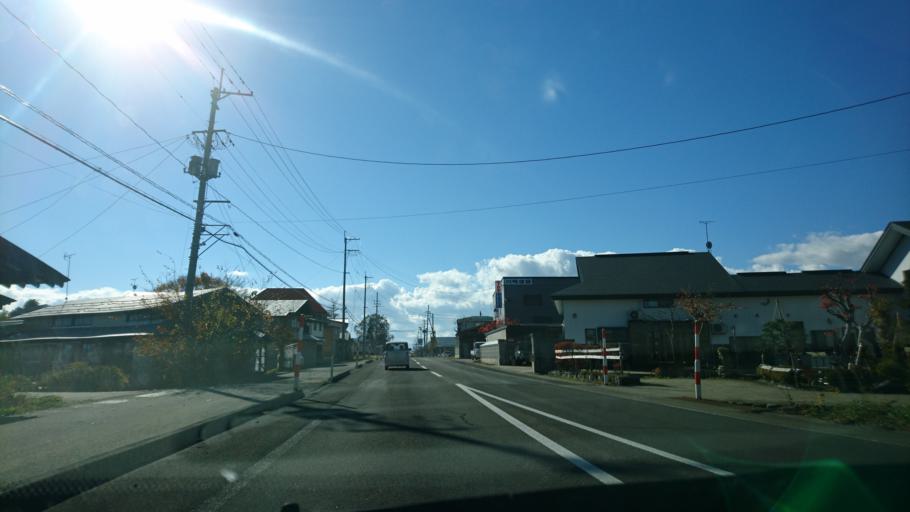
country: JP
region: Akita
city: Yokotemachi
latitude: 39.2735
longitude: 140.5012
